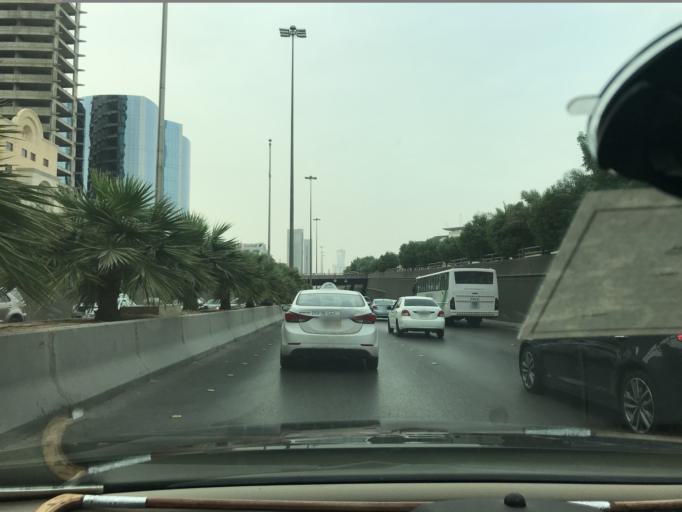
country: SA
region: Ar Riyad
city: Riyadh
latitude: 24.7099
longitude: 46.6729
